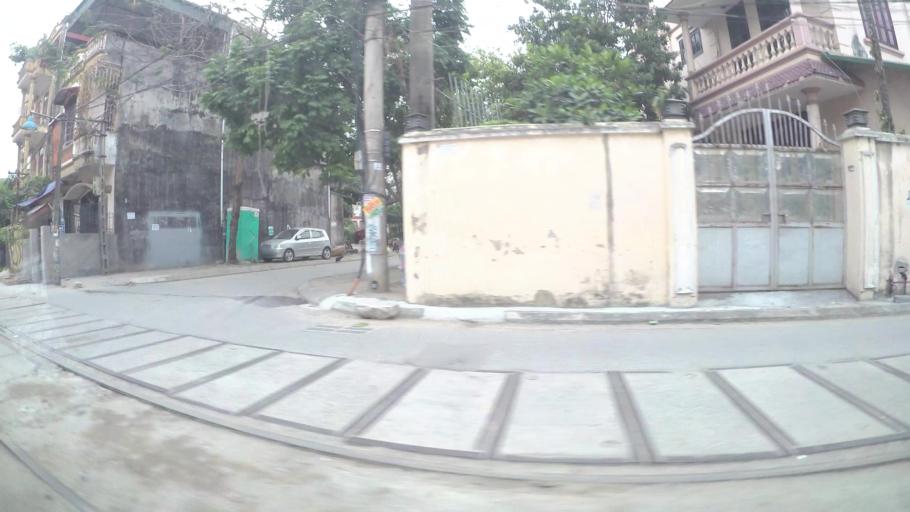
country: VN
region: Ha Noi
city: Hoan Kiem
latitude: 21.0630
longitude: 105.8929
